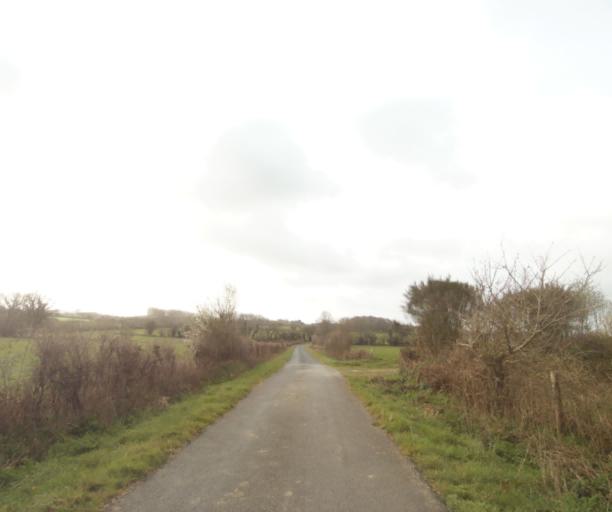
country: FR
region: Pays de la Loire
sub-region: Departement de la Loire-Atlantique
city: Bouvron
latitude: 47.4066
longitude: -1.8747
